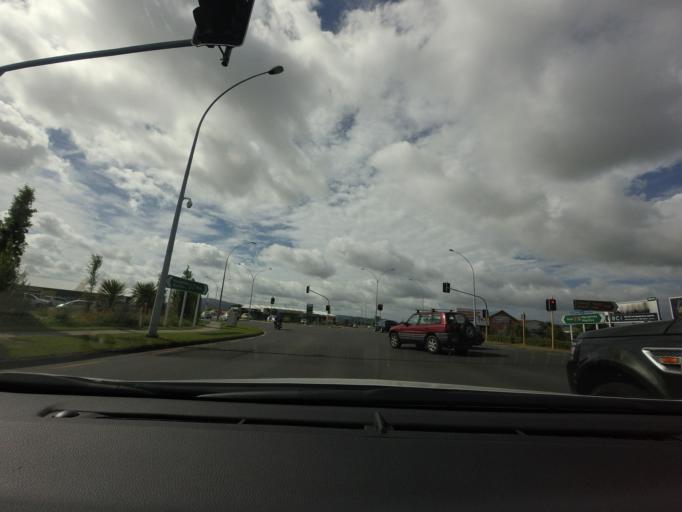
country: NZ
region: Bay of Plenty
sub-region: Rotorua District
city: Rotorua
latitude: -38.1247
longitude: 176.2312
